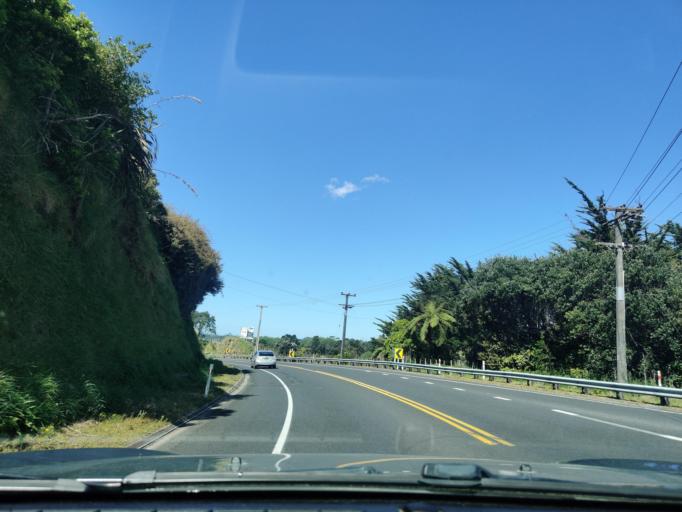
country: NZ
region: Taranaki
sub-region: New Plymouth District
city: New Plymouth
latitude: -39.1017
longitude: 174.0108
